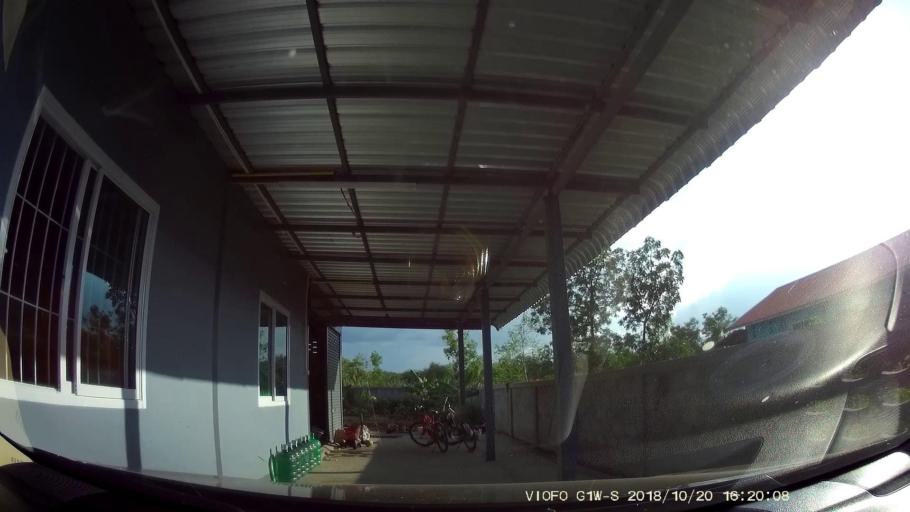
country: TH
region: Khon Kaen
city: Chum Phae
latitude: 16.4890
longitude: 102.1203
